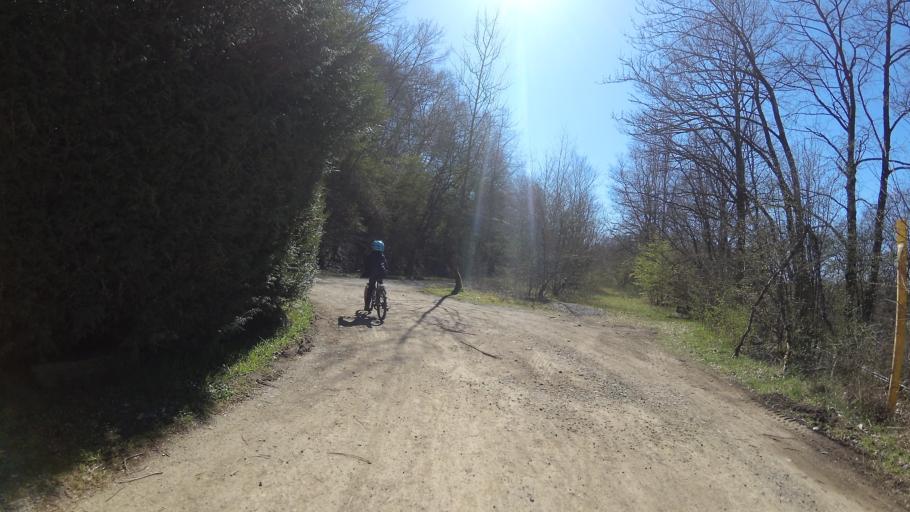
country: DE
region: Rheinland-Pfalz
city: Thallichtenberg
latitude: 49.5521
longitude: 7.3463
